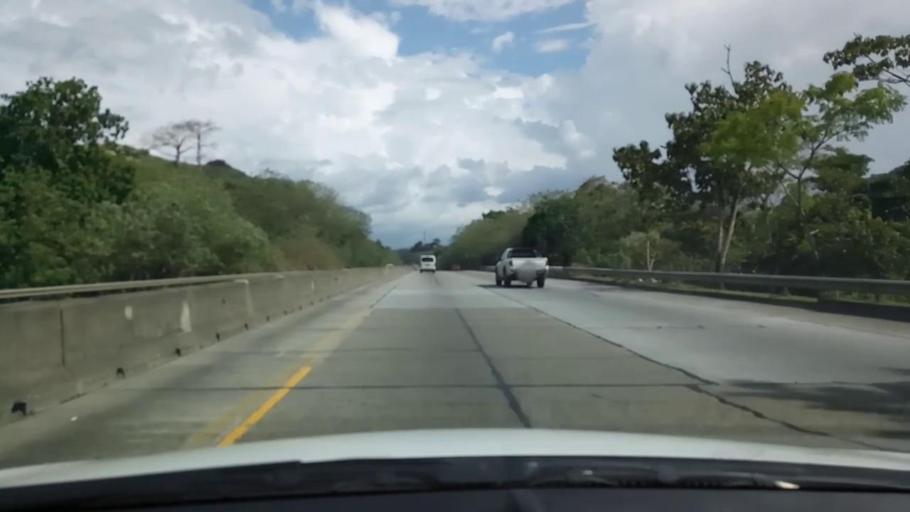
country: PA
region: Panama
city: Las Cumbres
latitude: 9.0684
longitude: -79.5693
